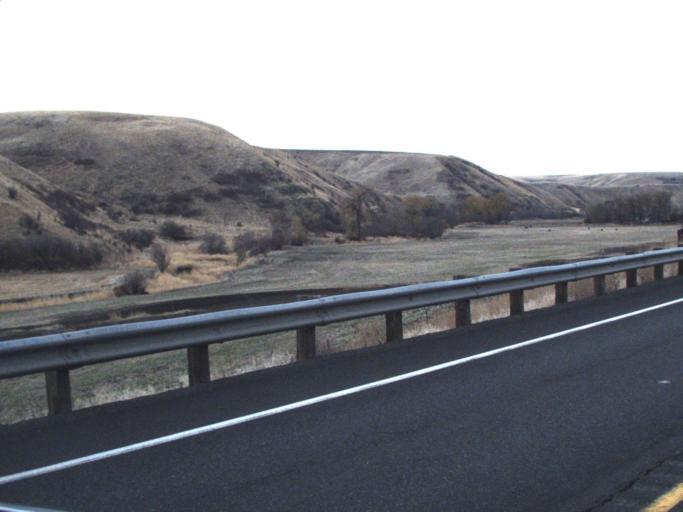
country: US
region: Washington
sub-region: Garfield County
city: Pomeroy
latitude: 46.4676
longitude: -117.4823
